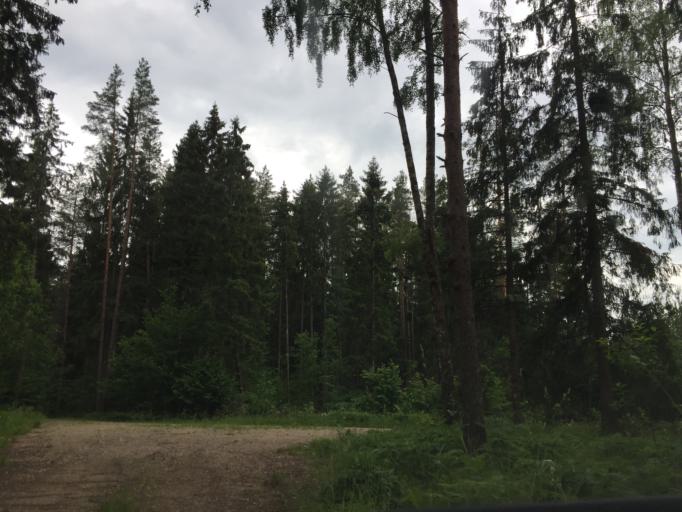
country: LV
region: Tukuma Rajons
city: Tukums
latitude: 57.0257
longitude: 23.0754
